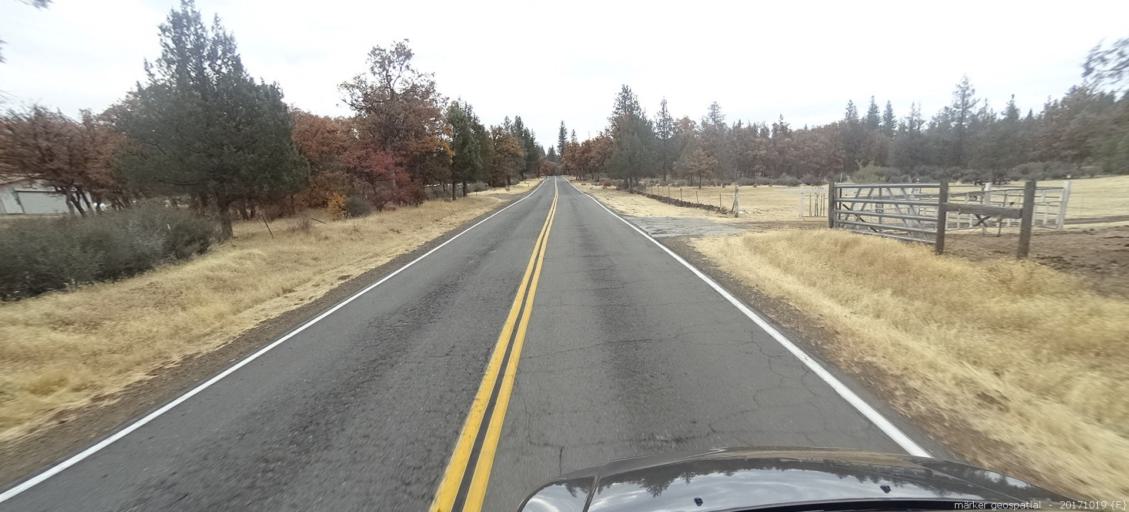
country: US
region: California
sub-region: Shasta County
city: Burney
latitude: 41.1296
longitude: -121.3387
